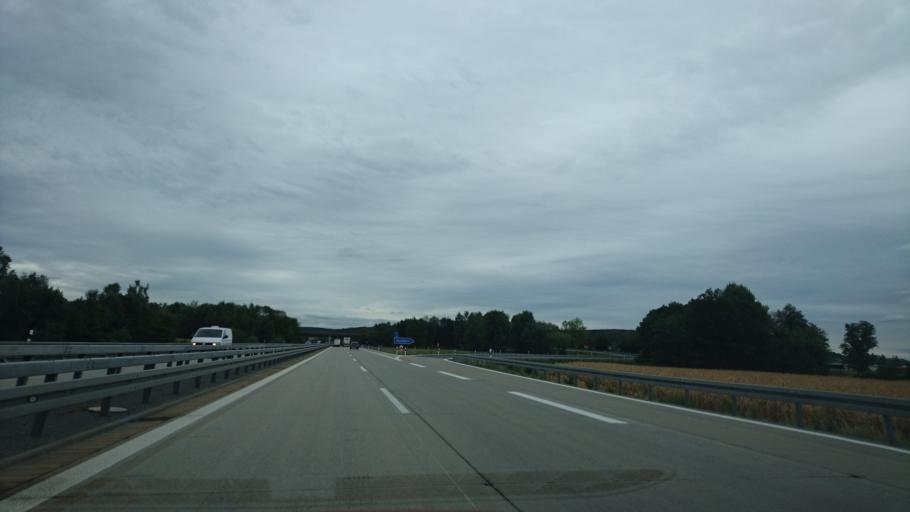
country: DE
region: Bavaria
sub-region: Upper Palatinate
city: Luhe-Wildenau
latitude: 49.5906
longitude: 12.1385
